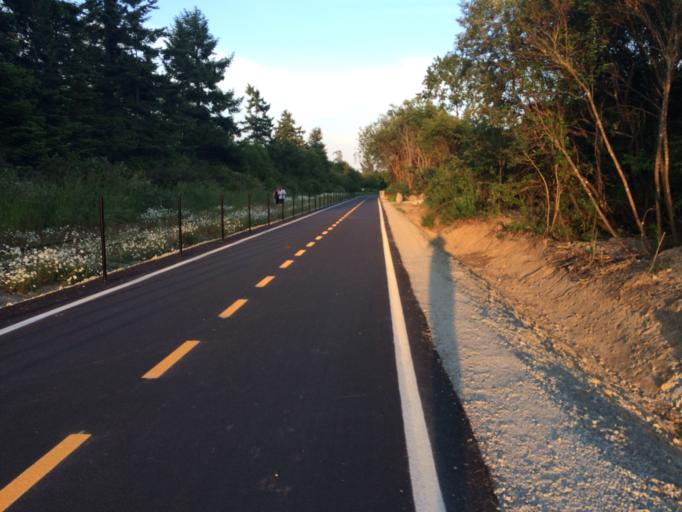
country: CA
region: British Columbia
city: Colwood
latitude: 48.4590
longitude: -123.4402
